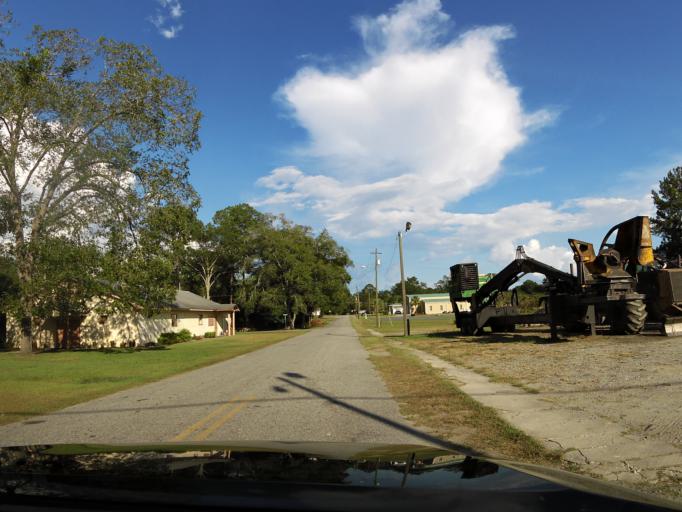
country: US
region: Georgia
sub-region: Brooks County
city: Quitman
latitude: 30.7754
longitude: -83.5604
